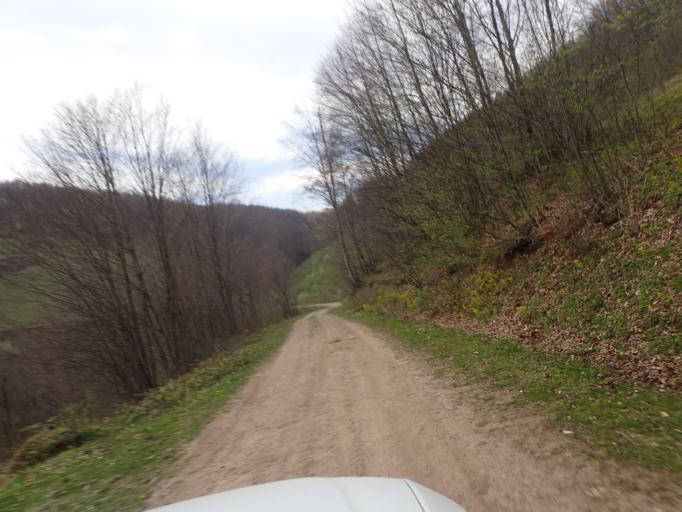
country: TR
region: Ordu
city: Aybasti
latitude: 40.7153
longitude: 37.2971
